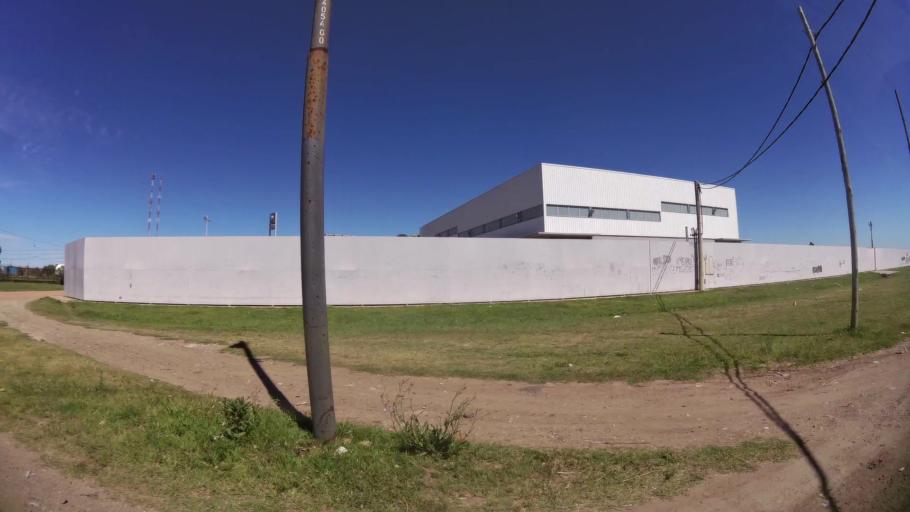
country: AR
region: Santa Fe
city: Perez
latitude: -32.9767
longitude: -60.7112
